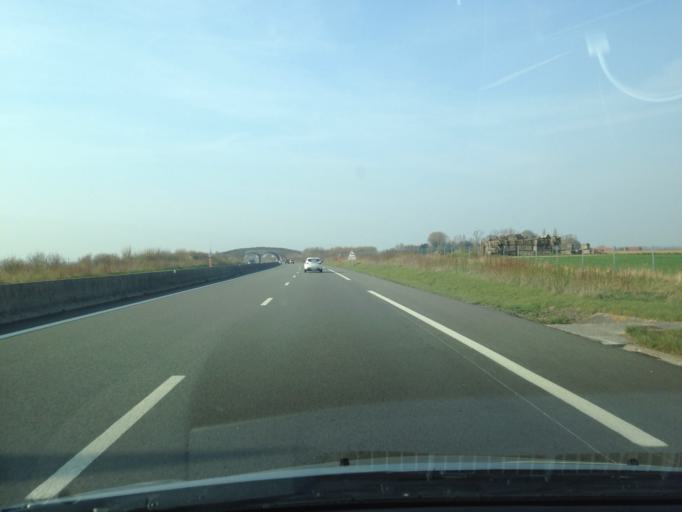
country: FR
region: Picardie
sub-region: Departement de la Somme
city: Nouvion
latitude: 50.2547
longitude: 1.7493
